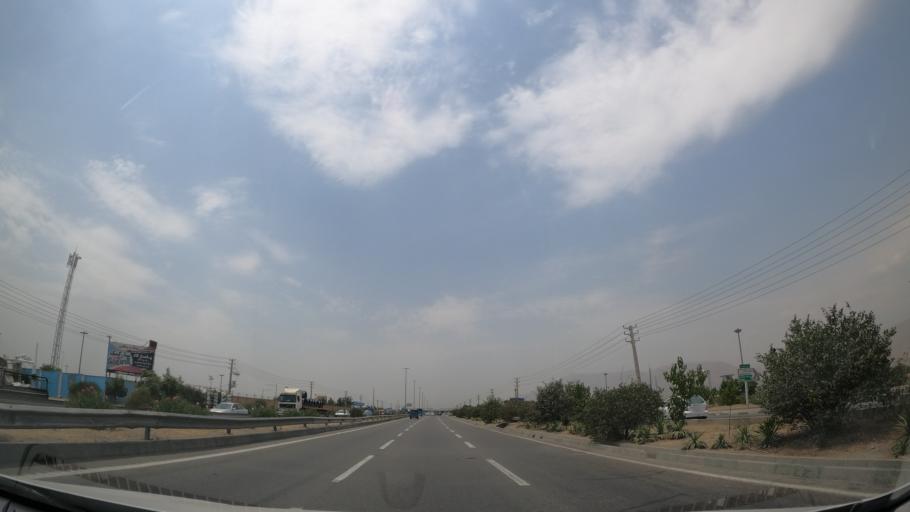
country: IR
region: Tehran
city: Shahr-e Qods
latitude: 35.6978
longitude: 51.1973
